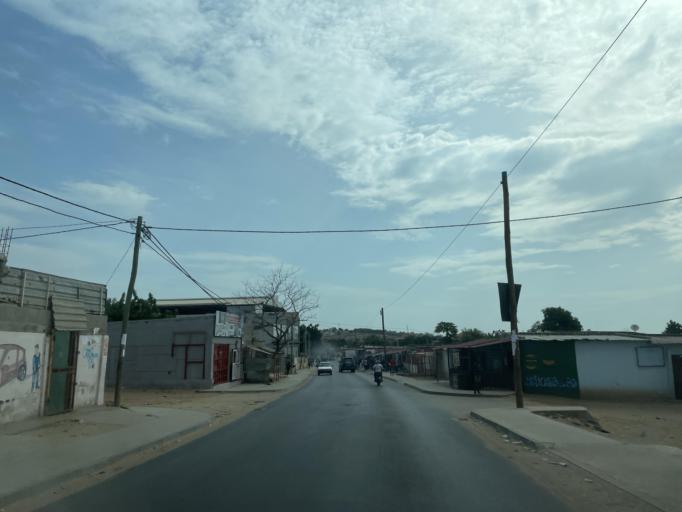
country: AO
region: Luanda
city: Luanda
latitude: -8.9314
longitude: 13.2015
